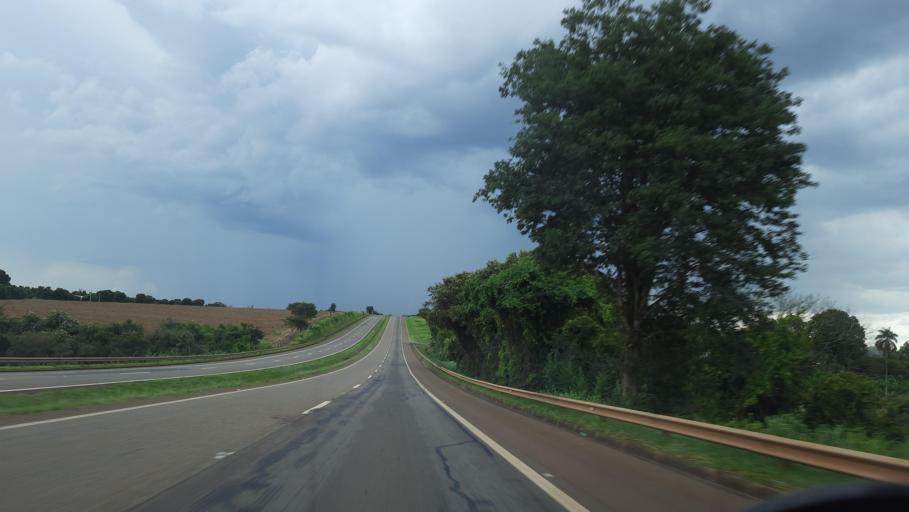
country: BR
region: Sao Paulo
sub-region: Aguai
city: Aguai
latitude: -22.0649
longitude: -47.0241
